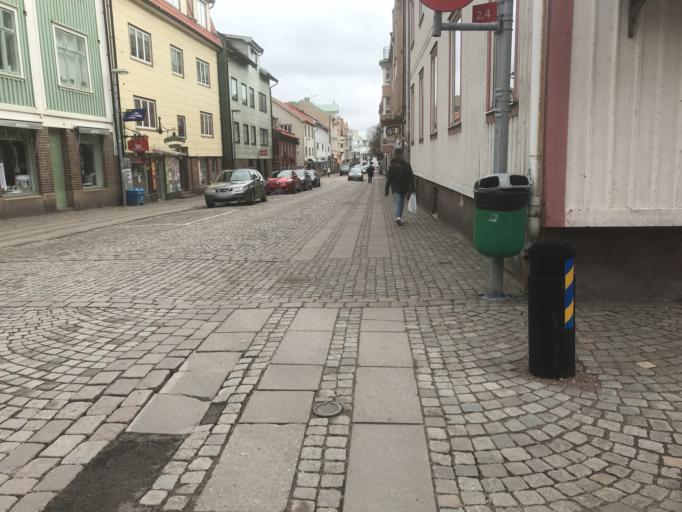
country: SE
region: Vaestra Goetaland
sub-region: Lysekils Kommun
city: Lysekil
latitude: 58.2749
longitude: 11.4320
